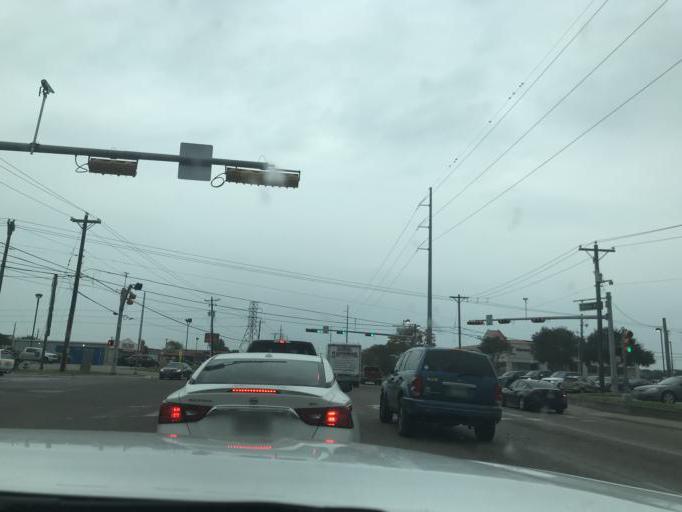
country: US
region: Texas
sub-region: Nueces County
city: Corpus Christi
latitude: 27.6922
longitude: -97.3638
